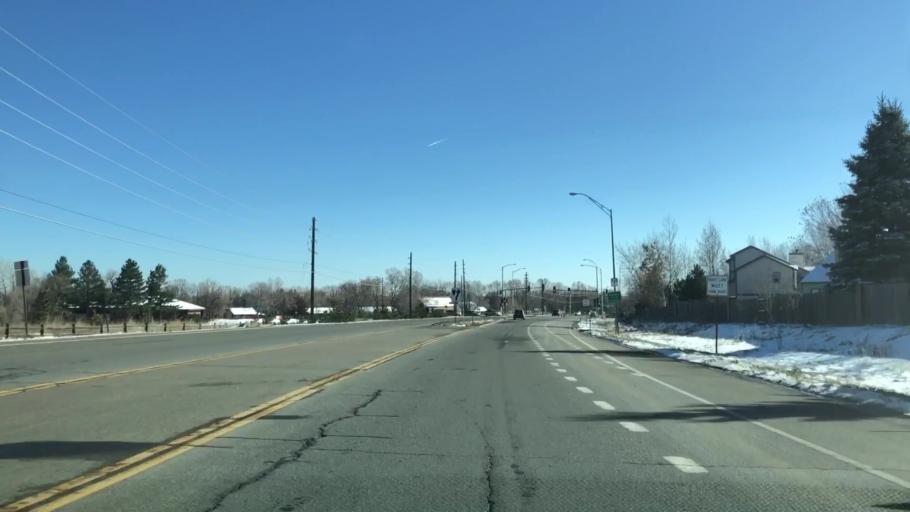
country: US
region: Colorado
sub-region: Boulder County
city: Boulder
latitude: 40.0524
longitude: -105.2616
